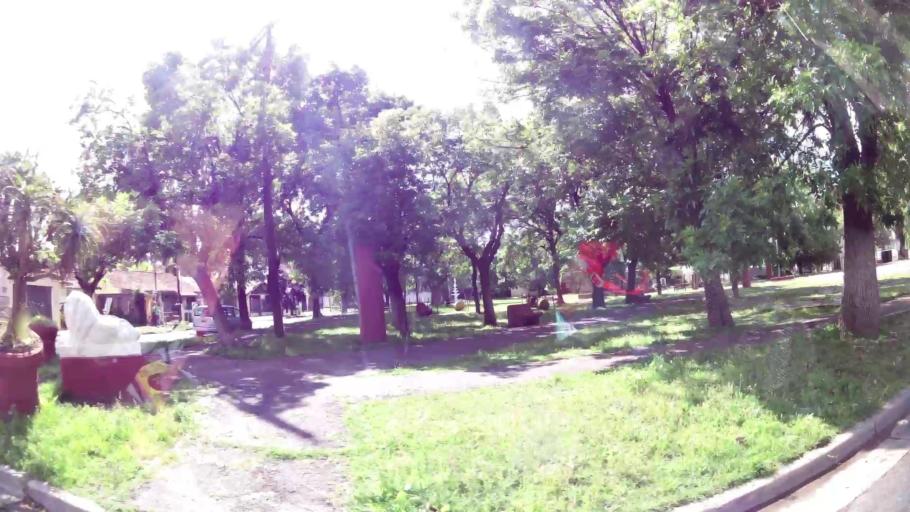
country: AR
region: Buenos Aires
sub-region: Partido de Lanus
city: Lanus
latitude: -34.6783
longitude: -58.4160
